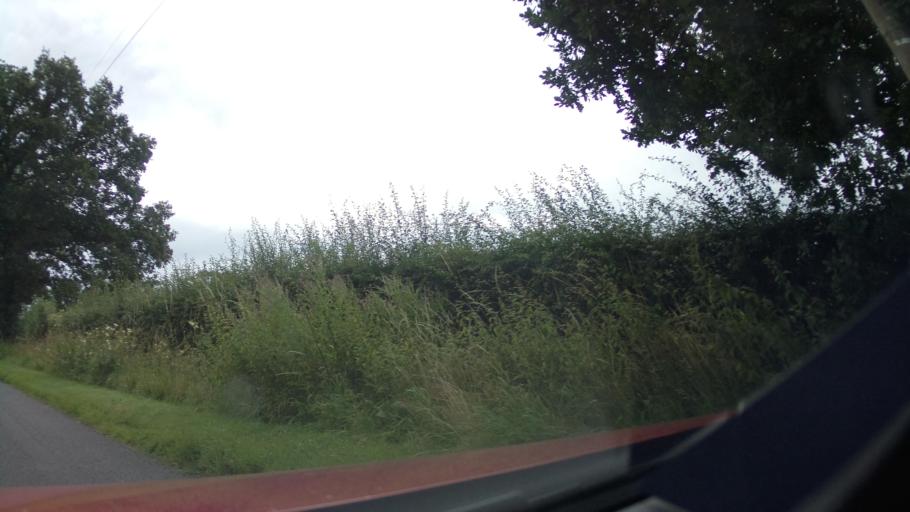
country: GB
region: England
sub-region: Solihull
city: Dickens Heath
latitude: 52.3754
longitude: -1.8385
